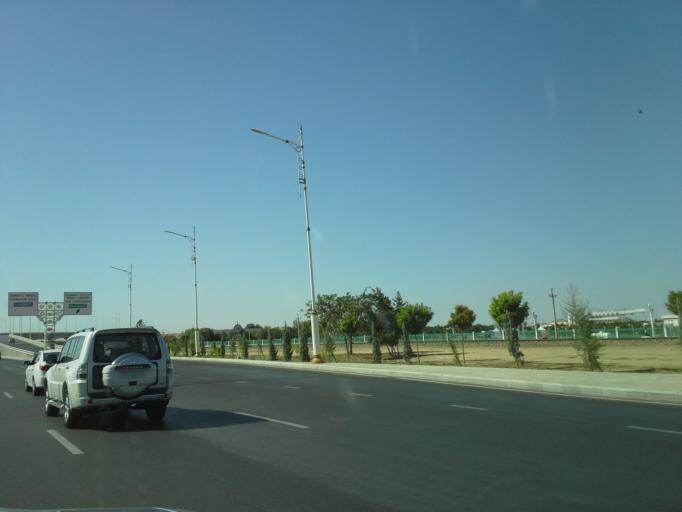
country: TM
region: Ahal
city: Ashgabat
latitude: 37.9239
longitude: 58.4374
